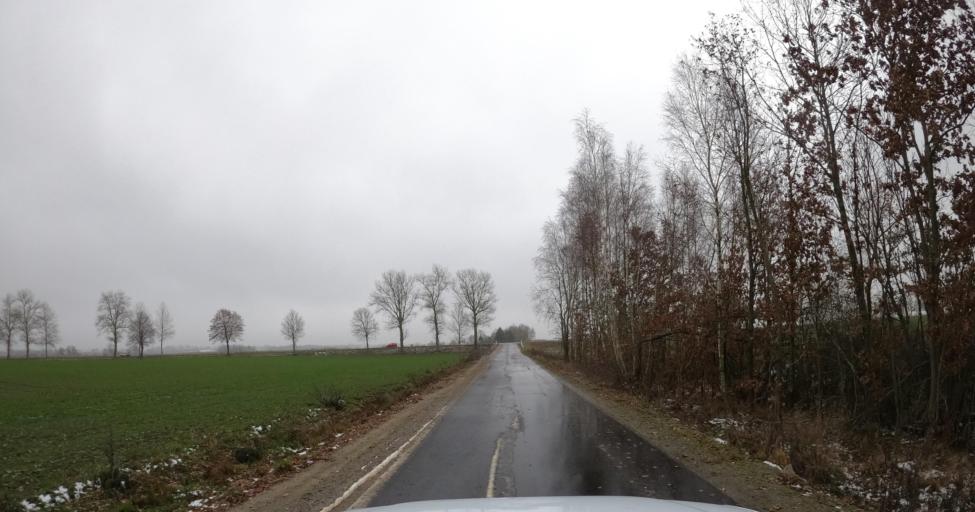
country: PL
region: West Pomeranian Voivodeship
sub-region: Powiat bialogardzki
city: Bialogard
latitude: 54.0310
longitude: 16.0355
